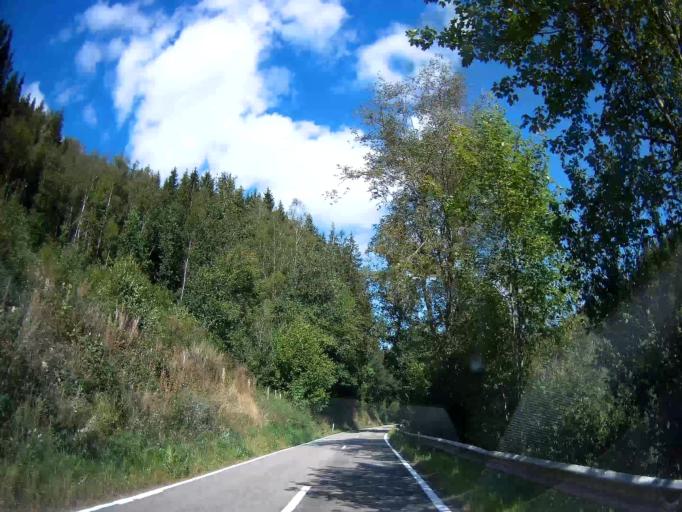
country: BE
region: Wallonia
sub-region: Province du Luxembourg
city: Bertogne
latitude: 50.0940
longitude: 5.6744
